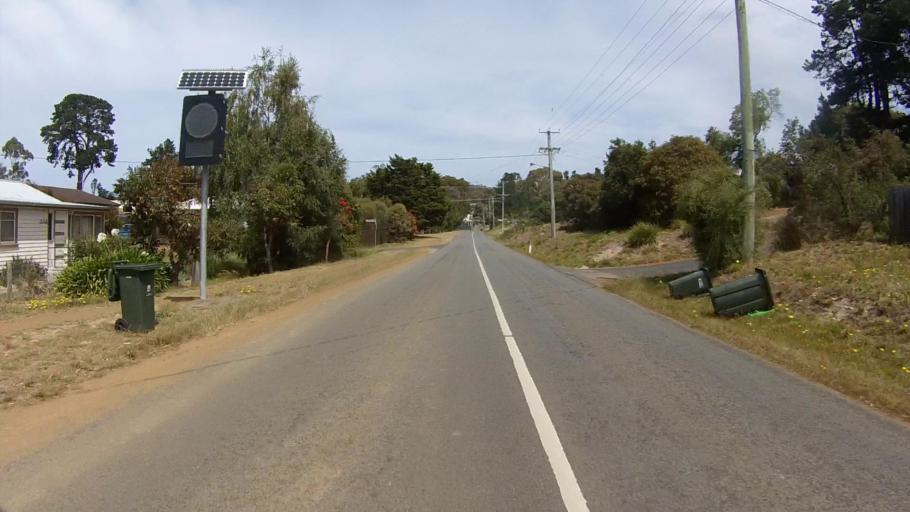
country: AU
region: Tasmania
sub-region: Kingborough
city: Blackmans Bay
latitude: -43.0249
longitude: 147.4177
